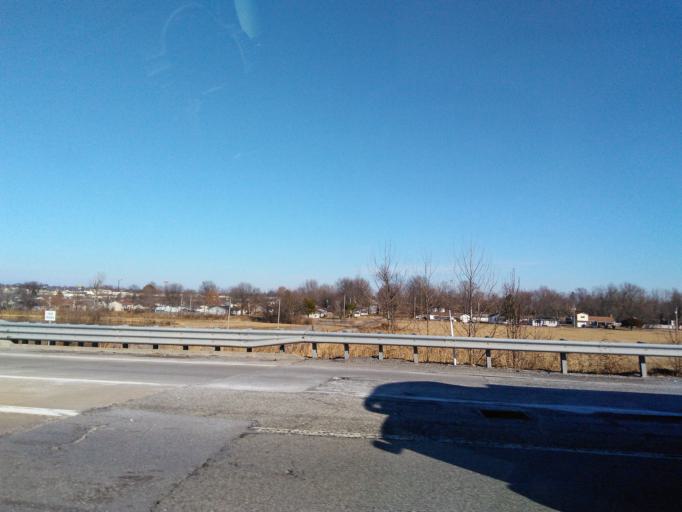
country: US
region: Illinois
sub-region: Williamson County
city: Marion
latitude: 37.7332
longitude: -88.9586
